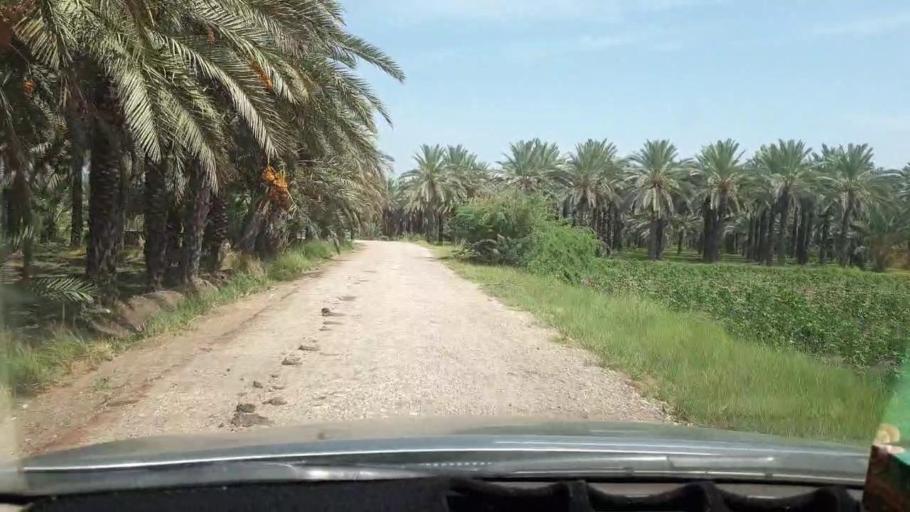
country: PK
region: Sindh
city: Khairpur
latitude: 27.4695
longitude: 68.7485
